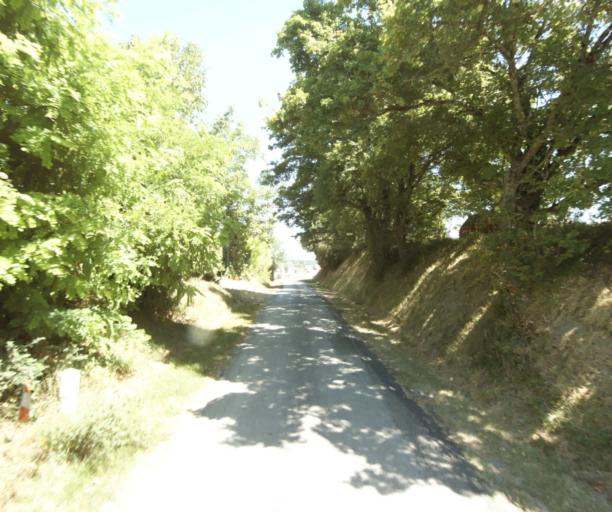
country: FR
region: Midi-Pyrenees
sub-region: Departement de la Haute-Garonne
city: Saint-Felix-Lauragais
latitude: 43.4798
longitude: 1.9226
